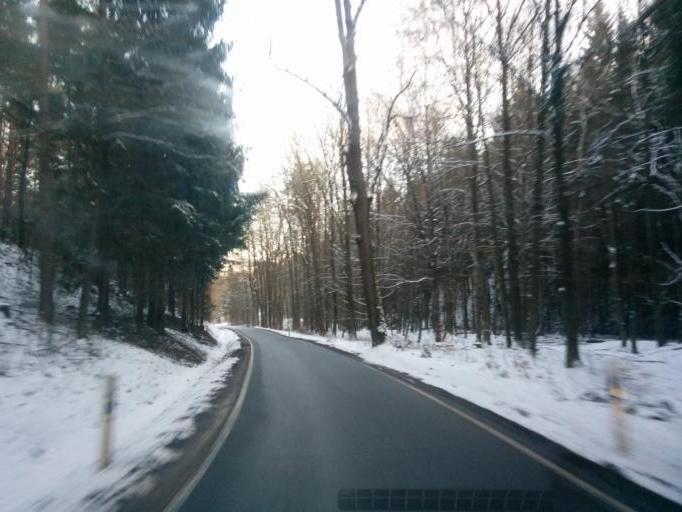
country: DE
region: Saxony
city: Floha
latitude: 50.8419
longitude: 13.0652
